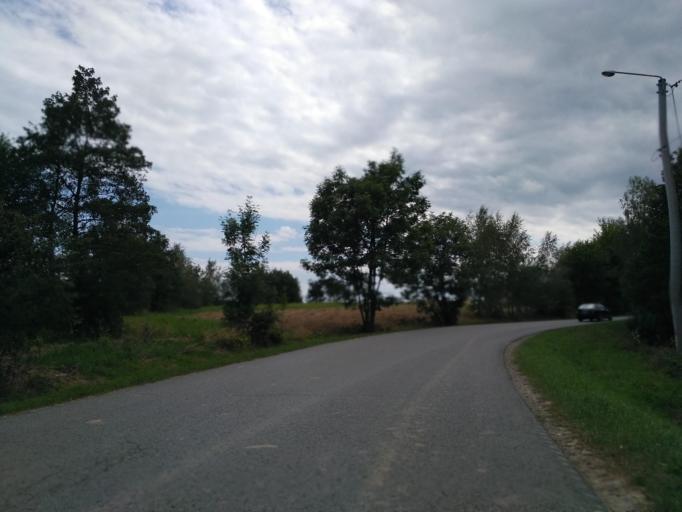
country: PL
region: Subcarpathian Voivodeship
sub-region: Powiat rzeszowski
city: Straszydle
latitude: 49.8838
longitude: 21.9918
